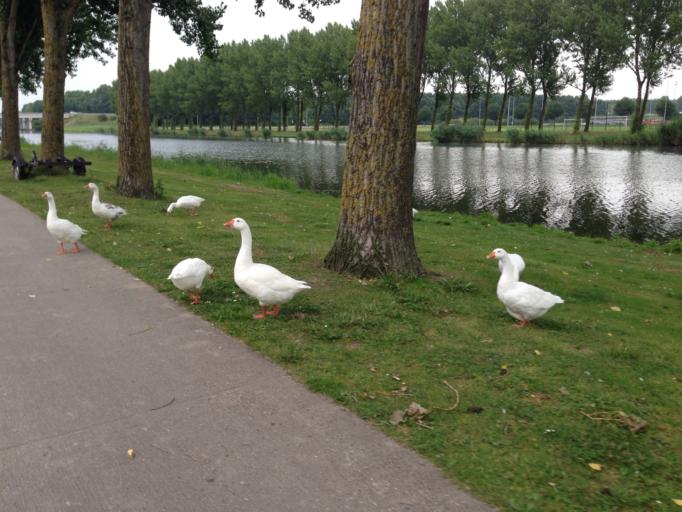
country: NL
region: Flevoland
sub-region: Gemeente Almere
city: Almere Stad
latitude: 52.3919
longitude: 5.2370
